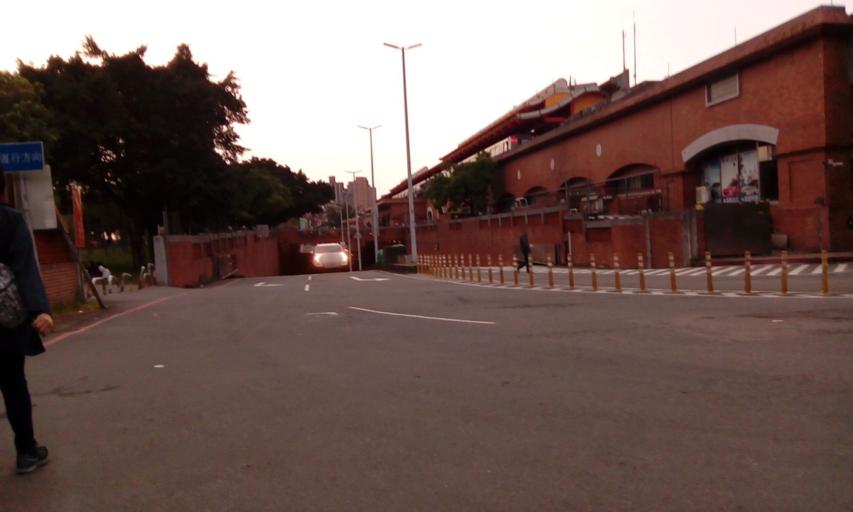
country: TW
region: Taipei
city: Taipei
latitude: 25.1666
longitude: 121.4468
